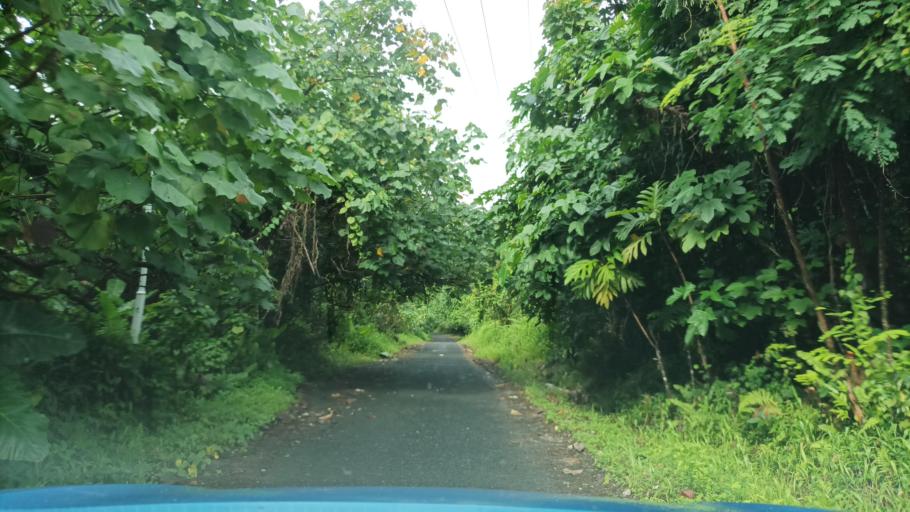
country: FM
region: Pohnpei
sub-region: Kolonia Municipality
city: Kolonia
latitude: 6.9240
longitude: 158.2850
